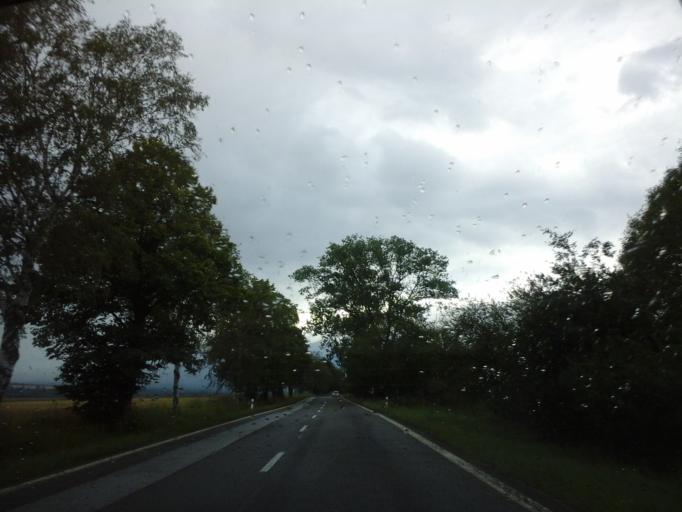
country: SK
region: Presovsky
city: Spisska Bela
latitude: 49.1989
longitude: 20.4234
